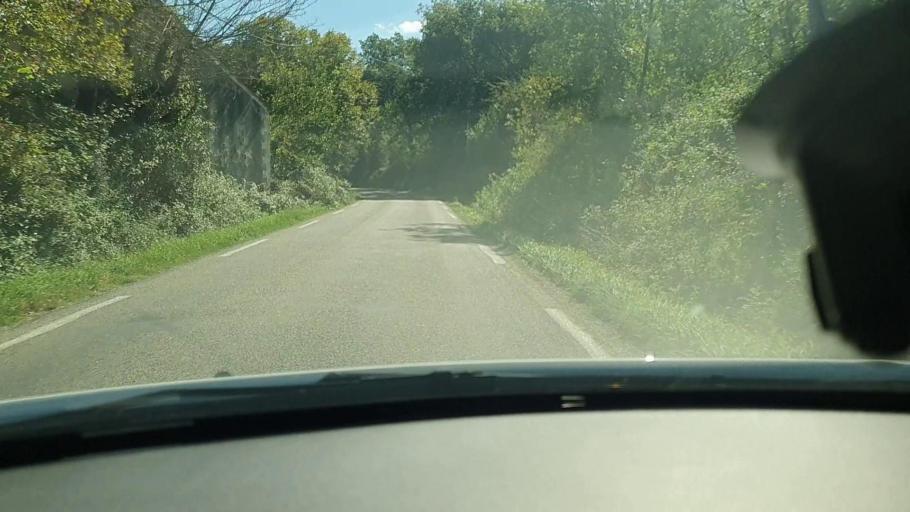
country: FR
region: Languedoc-Roussillon
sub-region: Departement du Gard
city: Goudargues
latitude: 44.1792
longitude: 4.4783
